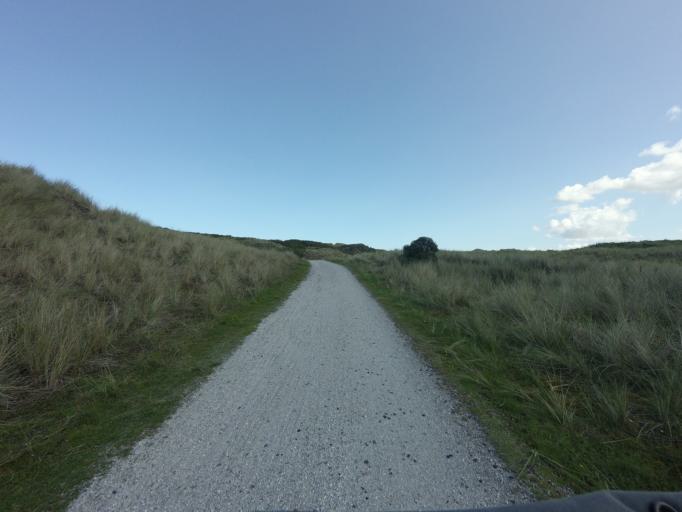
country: NL
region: Friesland
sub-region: Gemeente Terschelling
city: West-Terschelling
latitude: 53.4071
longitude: 5.3014
